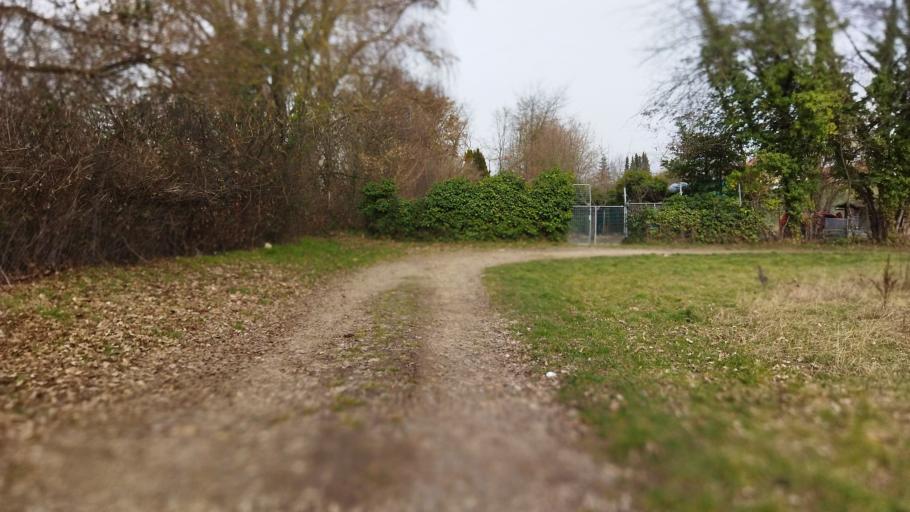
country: DE
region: Baden-Wuerttemberg
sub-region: Regierungsbezirk Stuttgart
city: Heilbronn
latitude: 49.1483
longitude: 9.1875
